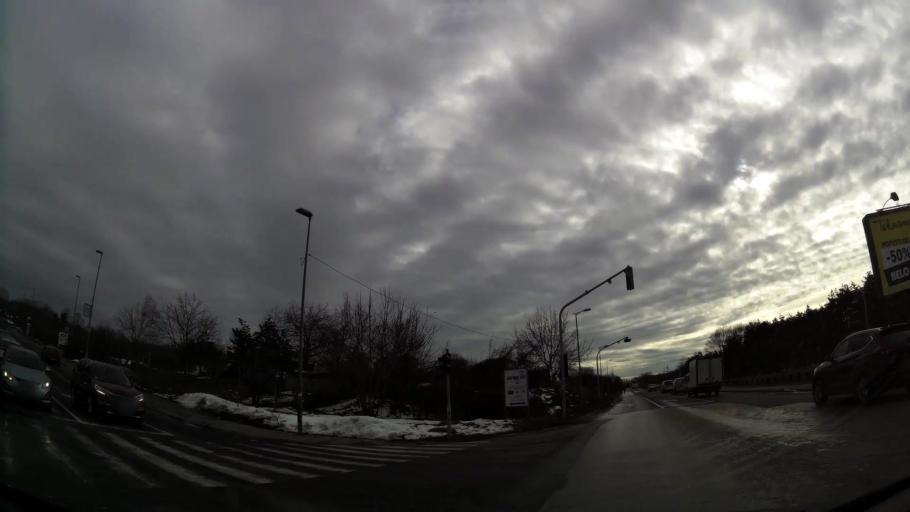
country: RS
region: Central Serbia
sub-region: Belgrade
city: Rakovica
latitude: 44.7489
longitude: 20.4121
